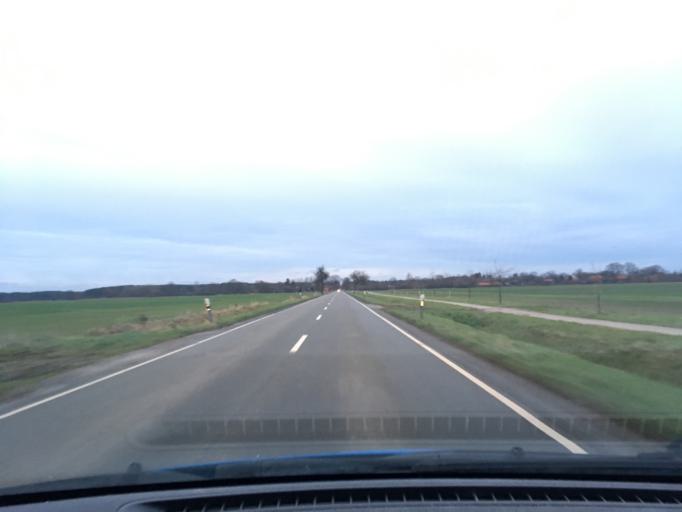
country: DE
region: Lower Saxony
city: Neu Darchau
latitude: 53.2525
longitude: 10.9092
